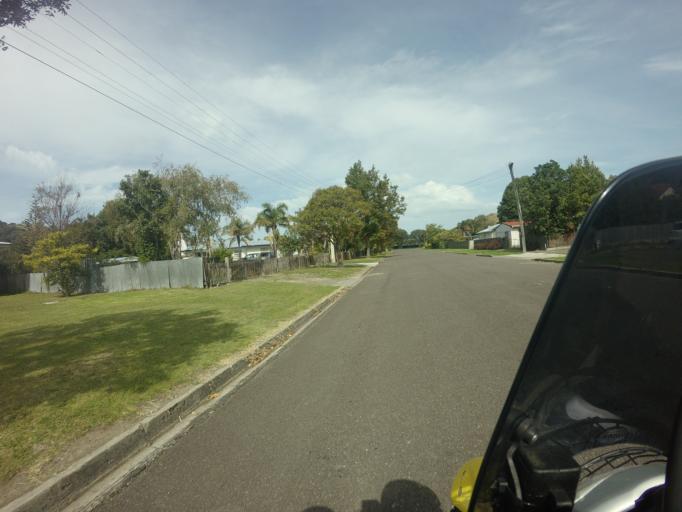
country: NZ
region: Gisborne
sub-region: Gisborne District
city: Gisborne
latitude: -38.6818
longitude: 178.0528
